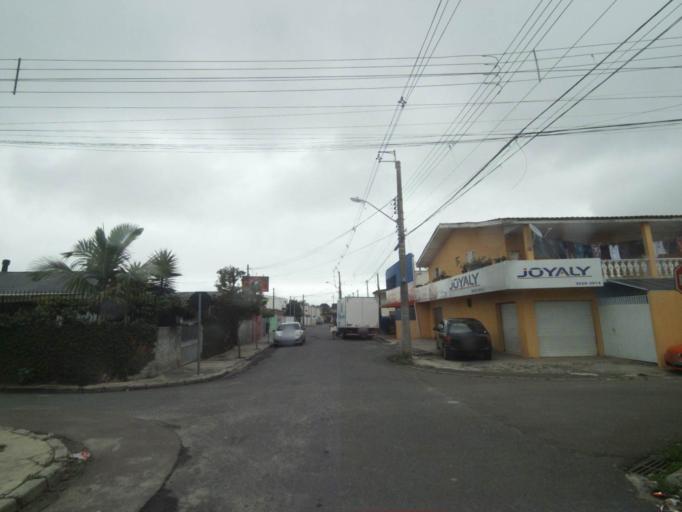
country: BR
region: Parana
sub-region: Curitiba
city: Curitiba
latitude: -25.4846
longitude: -49.3062
